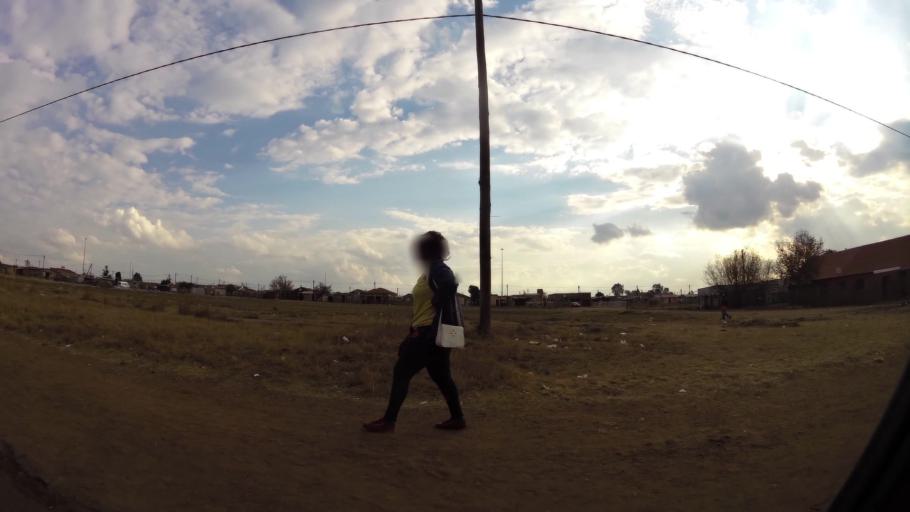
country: ZA
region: Gauteng
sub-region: Sedibeng District Municipality
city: Vanderbijlpark
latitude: -26.6743
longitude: 27.8684
